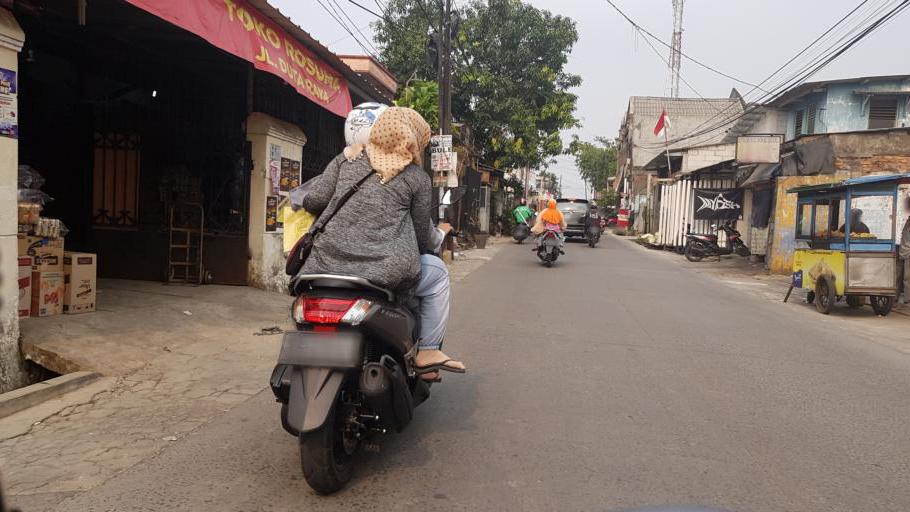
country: ID
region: West Java
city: Depok
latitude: -6.3723
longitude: 106.8497
